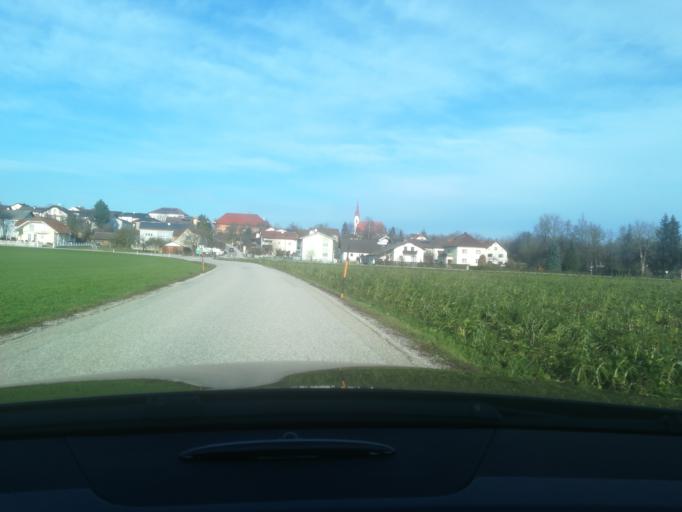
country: AT
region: Upper Austria
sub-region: Wels-Land
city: Holzhausen
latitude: 48.2194
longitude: 14.0985
